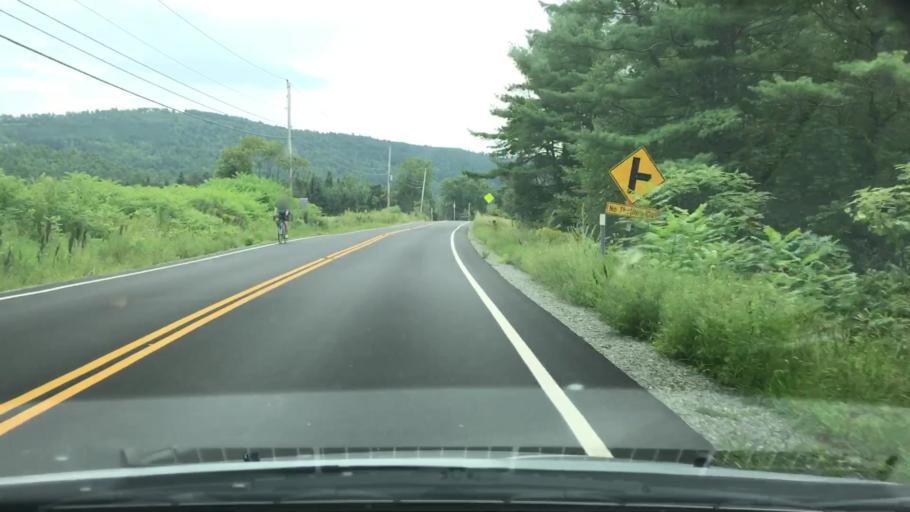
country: US
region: New Hampshire
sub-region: Grafton County
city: Lyme Town Offices
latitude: 43.8382
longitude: -72.1499
